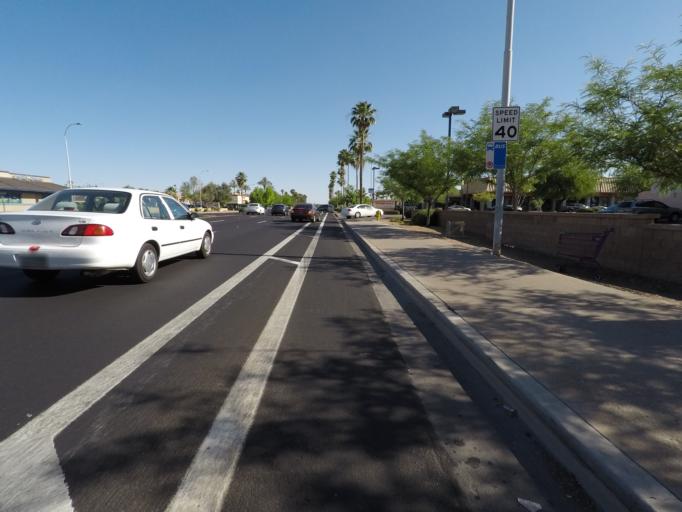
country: US
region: Arizona
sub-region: Maricopa County
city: Tempe
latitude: 33.3925
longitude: -111.9093
